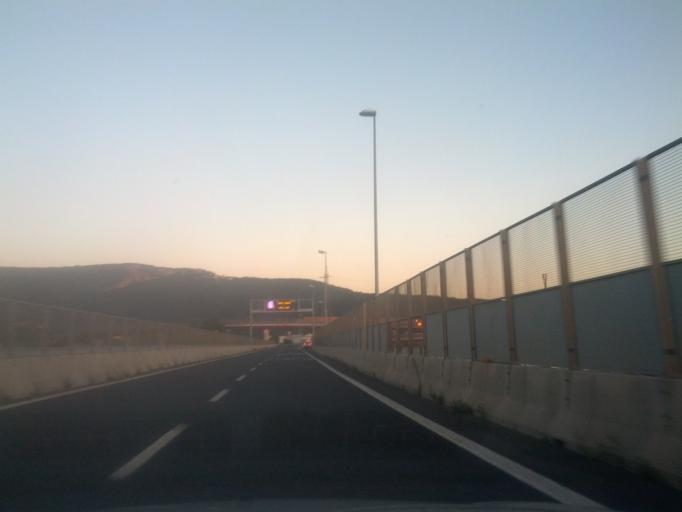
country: IT
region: Friuli Venezia Giulia
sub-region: Provincia di Trieste
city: Domio
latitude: 45.6111
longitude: 13.8277
